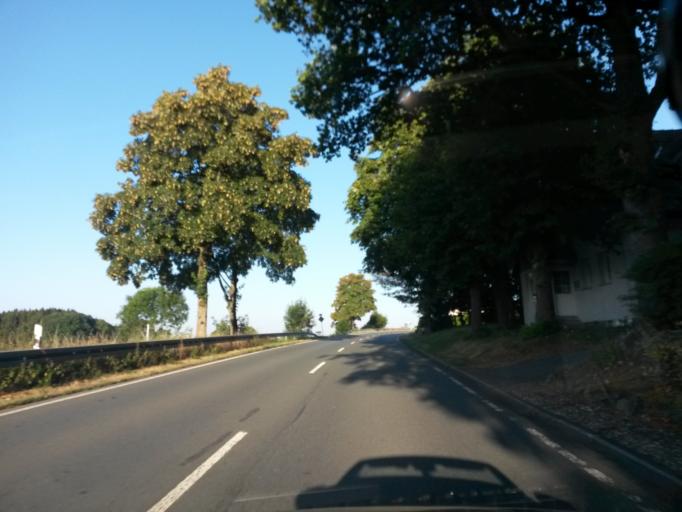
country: DE
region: North Rhine-Westphalia
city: Kierspe
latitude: 51.1194
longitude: 7.5695
